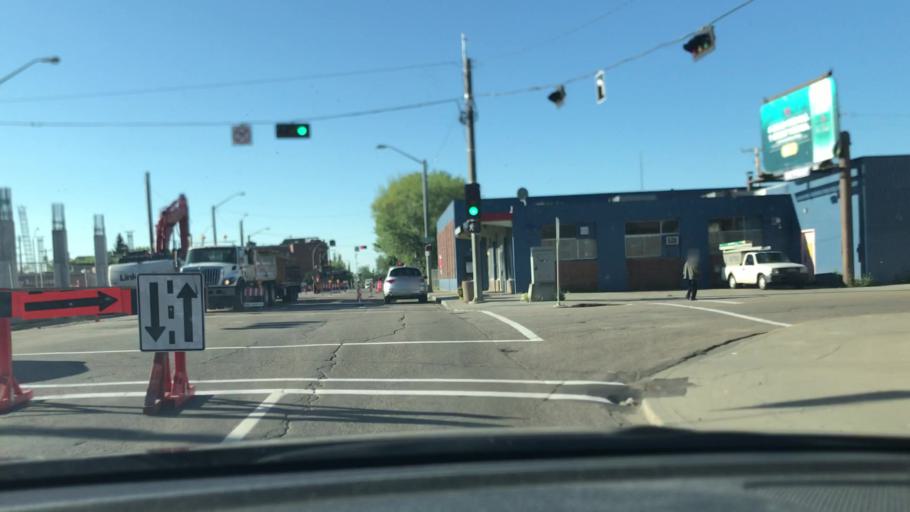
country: CA
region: Alberta
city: Edmonton
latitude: 53.5463
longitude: -113.4795
